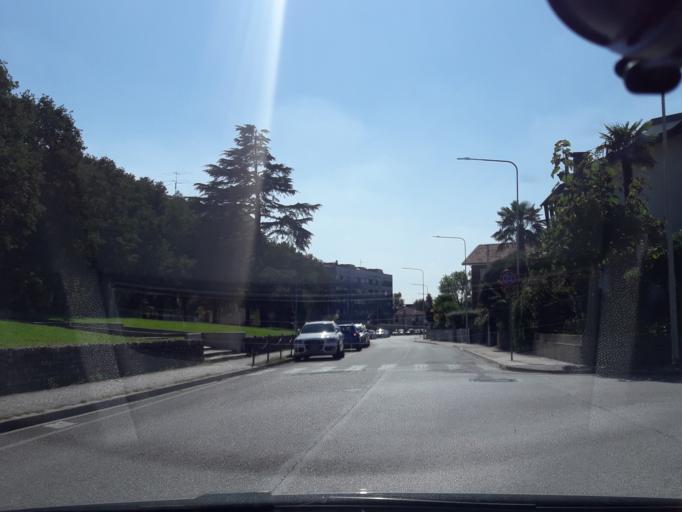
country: IT
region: Friuli Venezia Giulia
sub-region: Provincia di Udine
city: Udine
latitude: 46.0613
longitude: 13.2229
